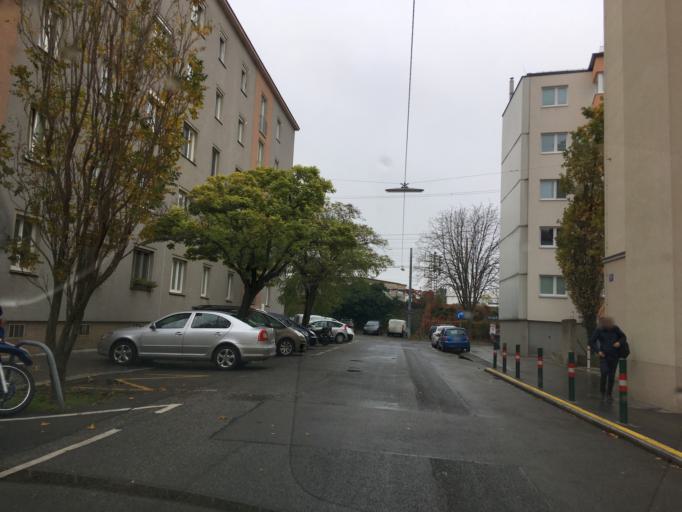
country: AT
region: Vienna
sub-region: Wien Stadt
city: Vienna
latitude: 48.2516
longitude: 16.3662
